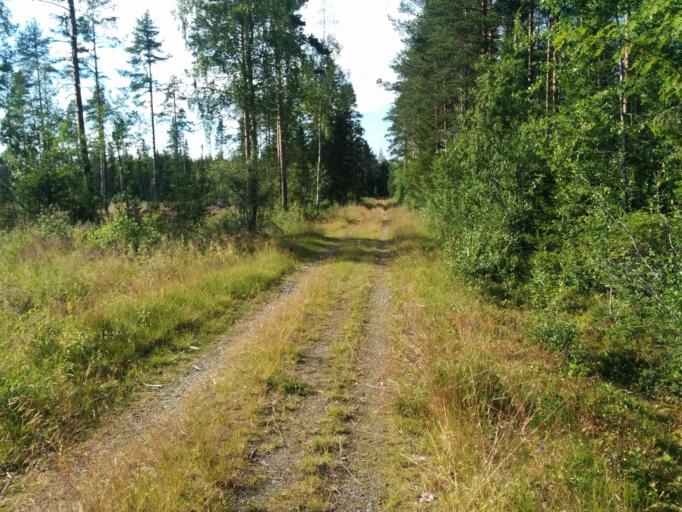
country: SE
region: Vaesterbotten
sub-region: Umea Kommun
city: Ersmark
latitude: 63.8872
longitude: 20.3040
